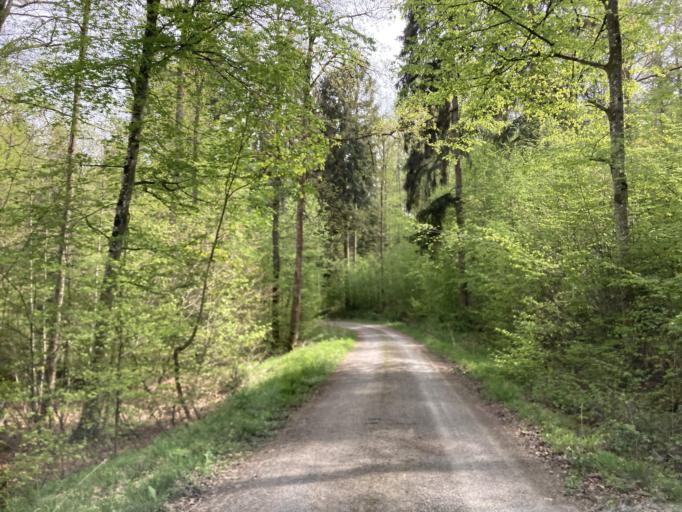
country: DE
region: Baden-Wuerttemberg
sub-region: Tuebingen Region
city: Rottenburg
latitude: 48.4572
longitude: 8.9826
